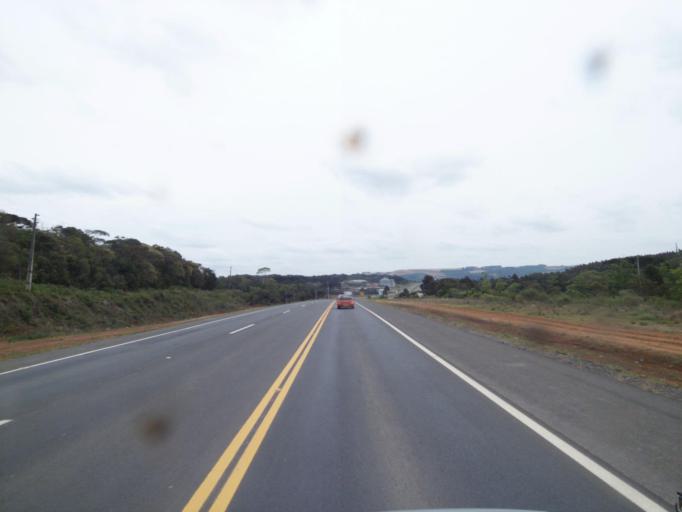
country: BR
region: Parana
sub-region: Irati
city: Irati
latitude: -25.4615
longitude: -50.5994
